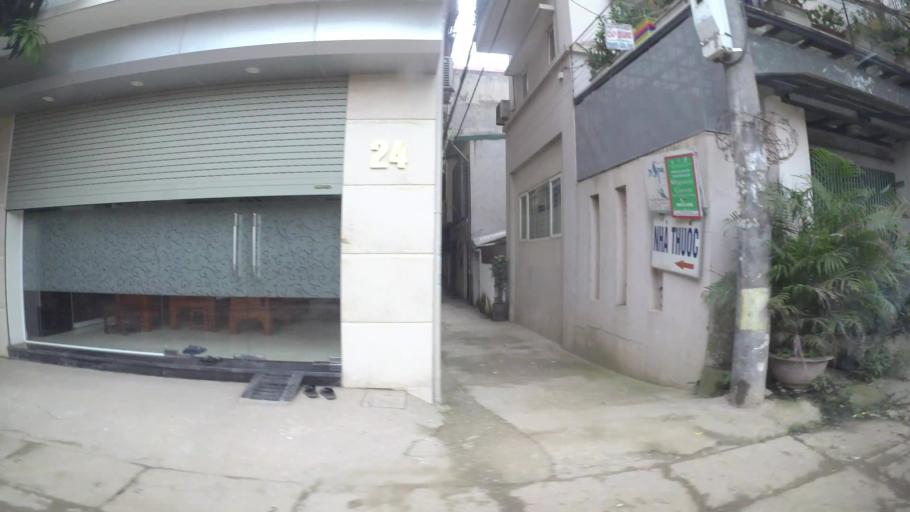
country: VN
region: Ha Noi
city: Tay Ho
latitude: 21.0667
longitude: 105.8355
